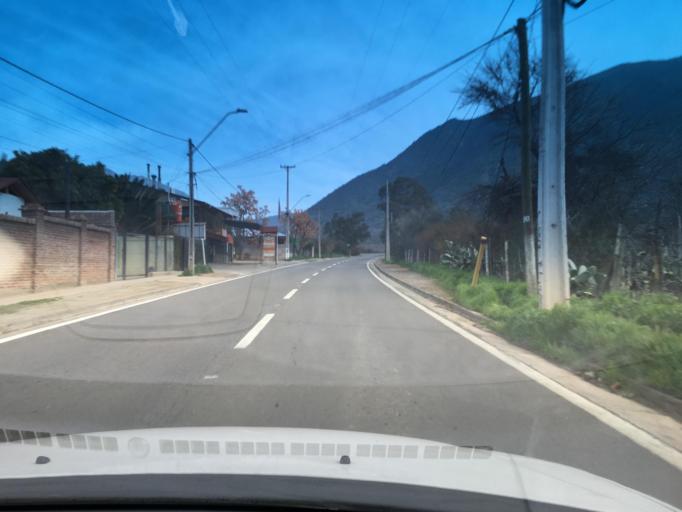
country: CL
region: Santiago Metropolitan
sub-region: Provincia de Chacabuco
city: Lampa
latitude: -33.0753
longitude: -70.9319
